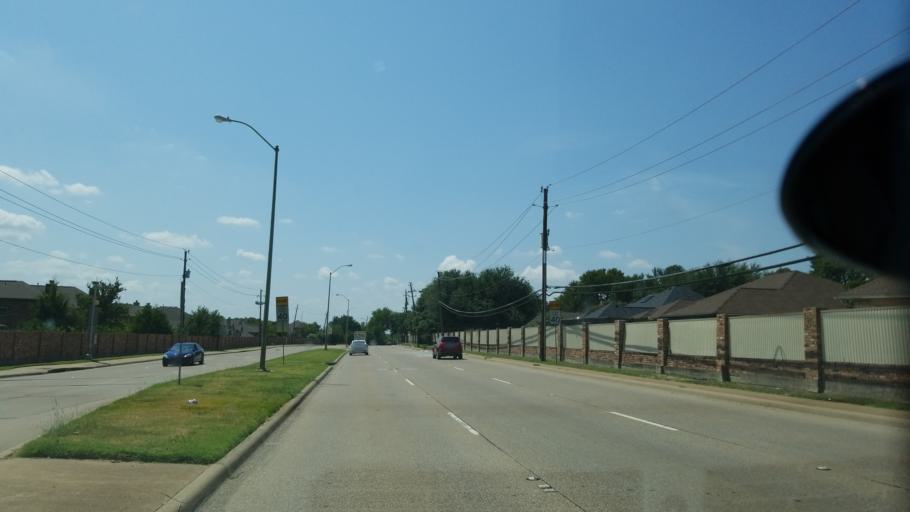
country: US
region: Texas
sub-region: Dallas County
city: Richardson
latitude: 32.9158
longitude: -96.7177
